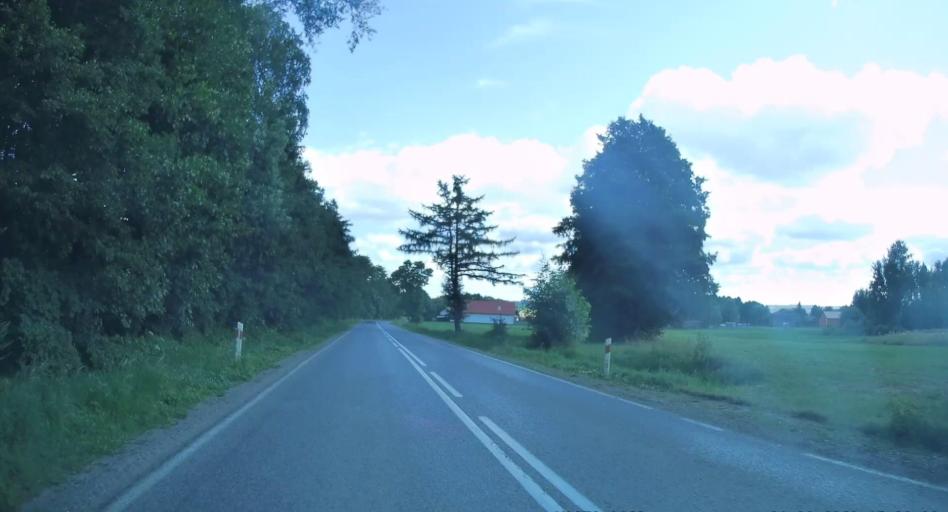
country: PL
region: Swietokrzyskie
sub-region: Powiat kielecki
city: Lagow
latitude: 50.8033
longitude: 21.0803
